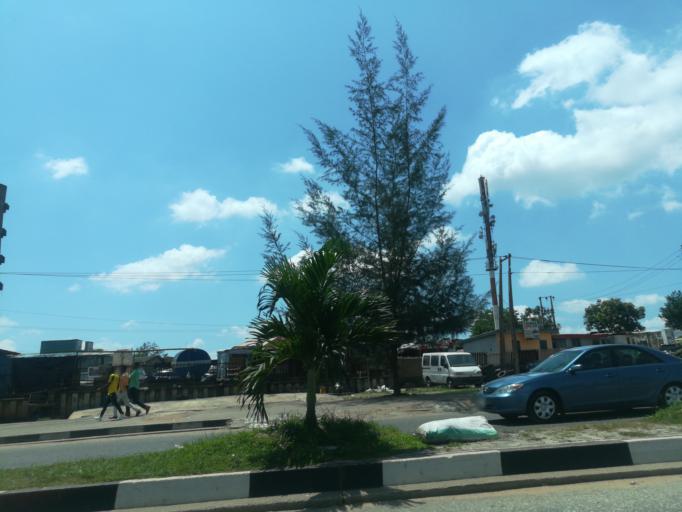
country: NG
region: Oyo
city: Ibadan
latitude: 7.3617
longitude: 3.8671
